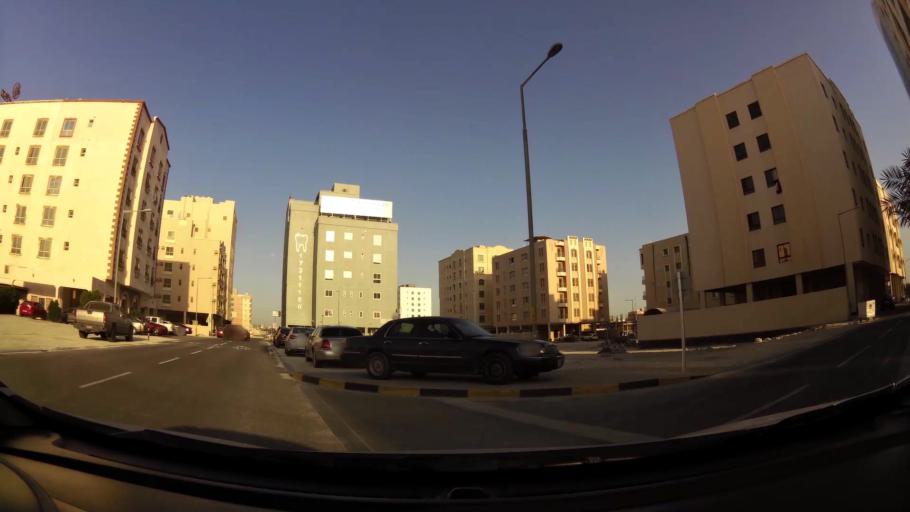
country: BH
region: Manama
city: Jidd Hafs
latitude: 26.2265
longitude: 50.5541
